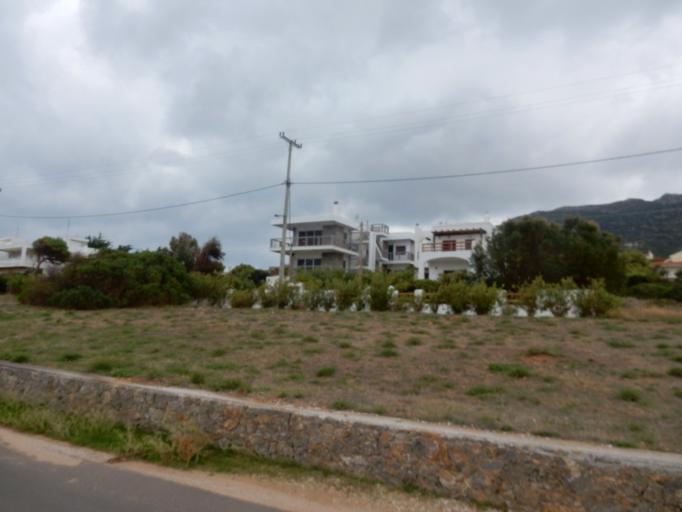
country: GR
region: Attica
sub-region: Nomarchia Anatolikis Attikis
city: Limin Mesoyaias
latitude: 37.9211
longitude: 24.0259
